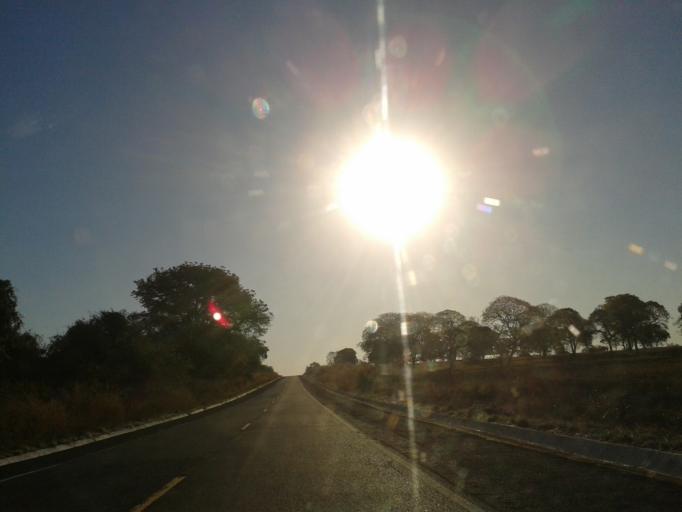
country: BR
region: Minas Gerais
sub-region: Santa Vitoria
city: Santa Vitoria
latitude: -19.1251
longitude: -50.2768
